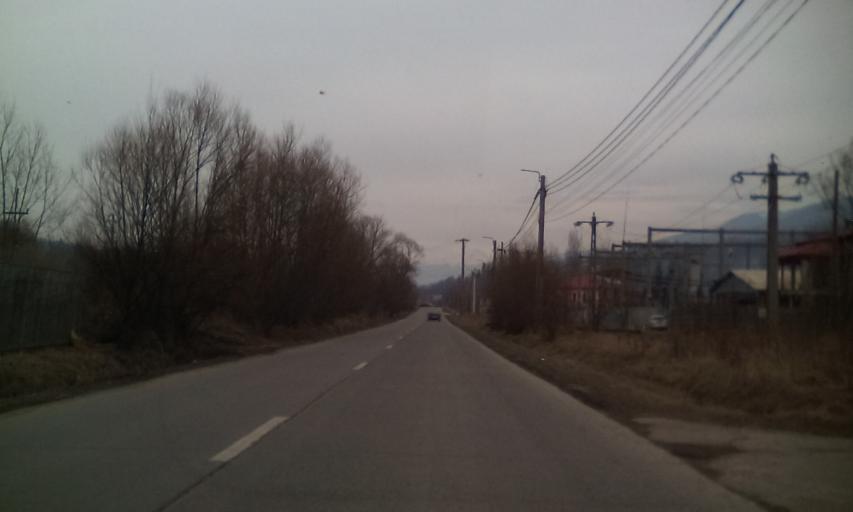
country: RO
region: Hunedoara
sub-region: Comuna Uricani
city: Uricani
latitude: 45.3374
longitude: 23.1395
